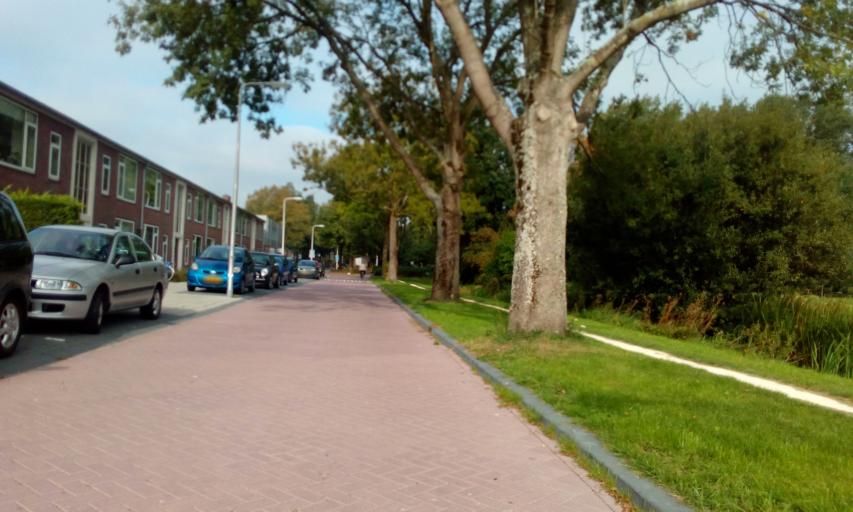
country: NL
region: South Holland
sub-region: Gemeente Voorschoten
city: Voorschoten
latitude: 52.1272
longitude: 4.4582
